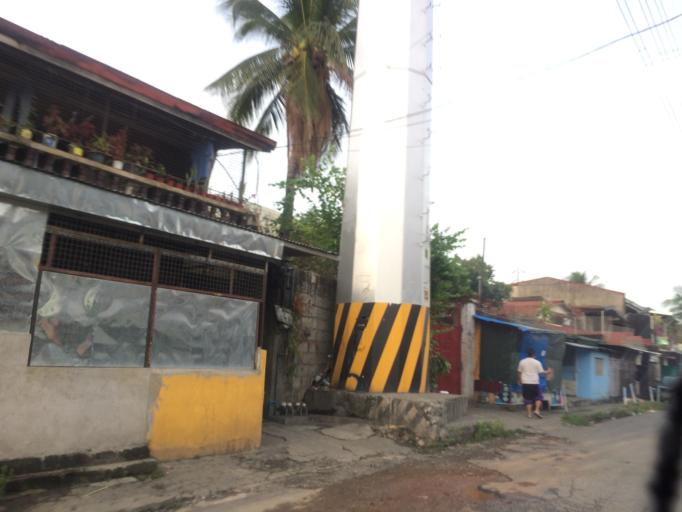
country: PH
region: Calabarzon
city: Del Monte
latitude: 14.6453
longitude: 121.0082
